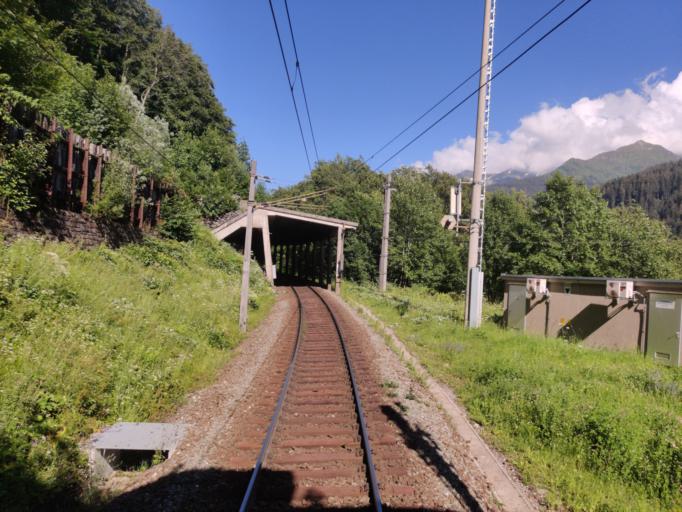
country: AT
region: Vorarlberg
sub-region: Politischer Bezirk Bludenz
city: Klosterle
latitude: 47.1327
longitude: 10.0751
